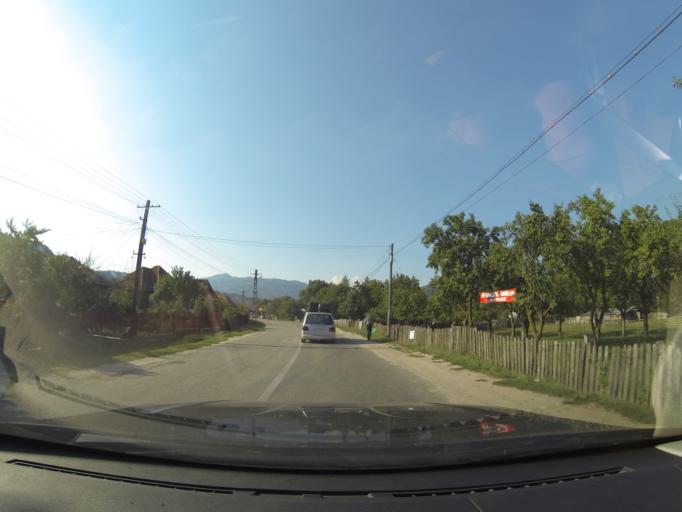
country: RO
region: Arges
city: Poenari
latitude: 45.3176
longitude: 24.6432
